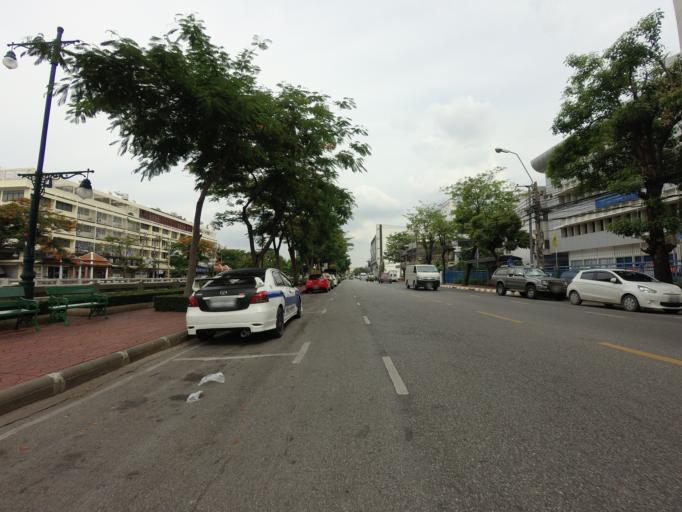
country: TH
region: Bangkok
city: Pom Prap Sattru Phai
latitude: 13.7587
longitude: 100.5142
